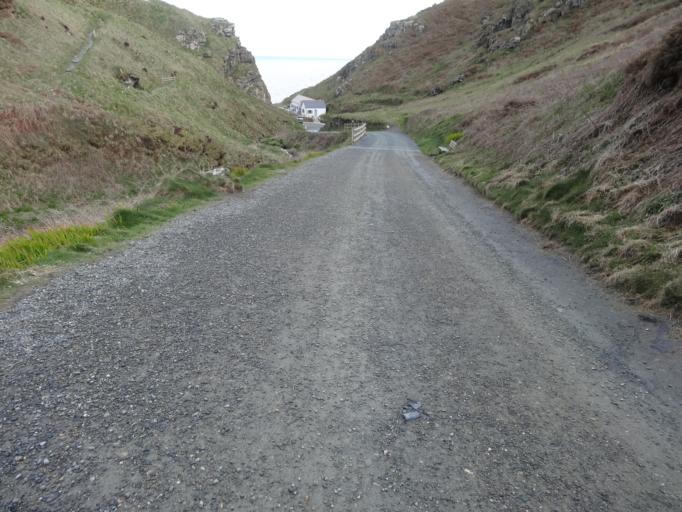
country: GB
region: England
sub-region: Cornwall
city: Tintagel
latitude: 50.6663
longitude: -4.7571
